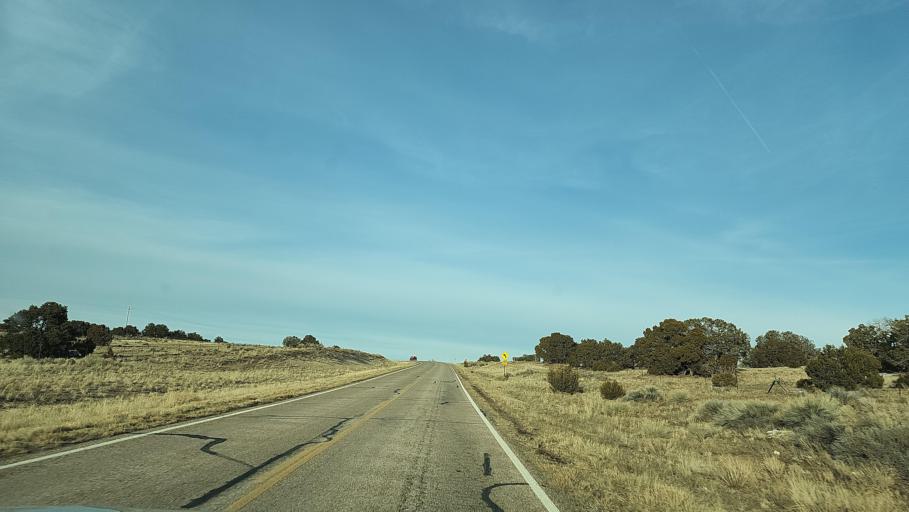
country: US
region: New Mexico
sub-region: Catron County
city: Reserve
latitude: 34.3870
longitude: -108.4516
